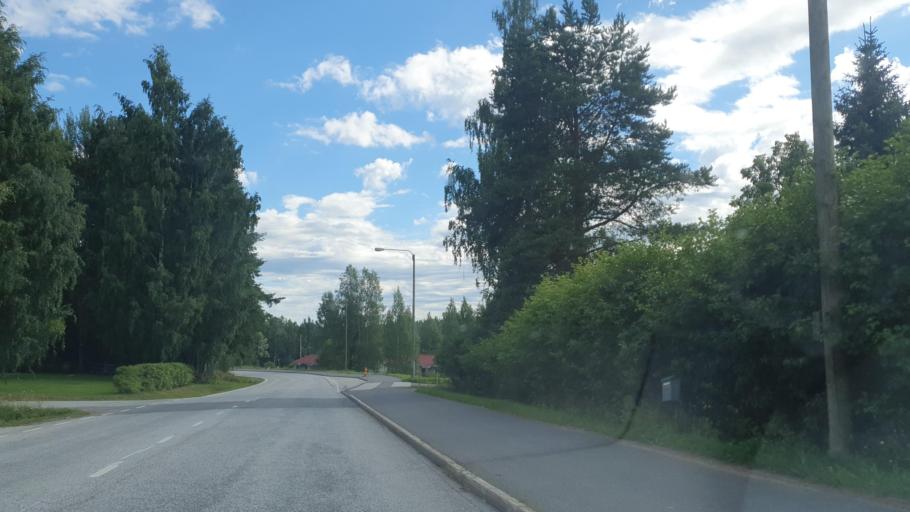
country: FI
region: Central Finland
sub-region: Jyvaeskylae
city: Saeynaetsalo
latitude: 62.1559
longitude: 25.7560
